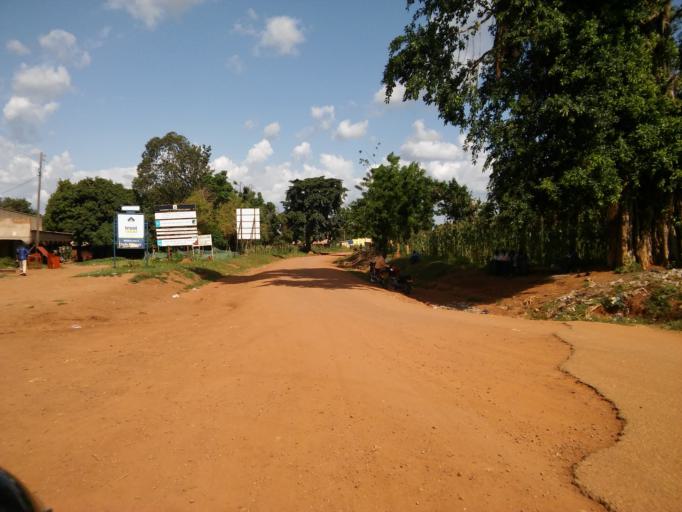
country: UG
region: Eastern Region
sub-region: Pallisa District
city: Pallisa
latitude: 1.1663
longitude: 33.7117
